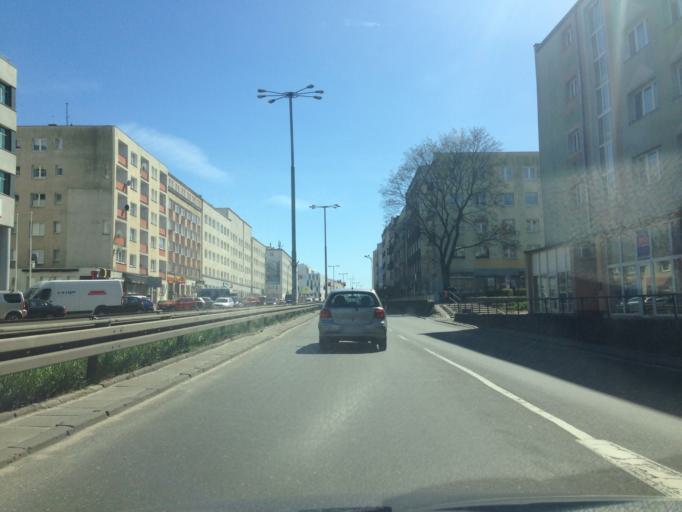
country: PL
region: Pomeranian Voivodeship
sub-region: Gdynia
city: Gdynia
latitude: 54.5165
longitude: 18.5318
